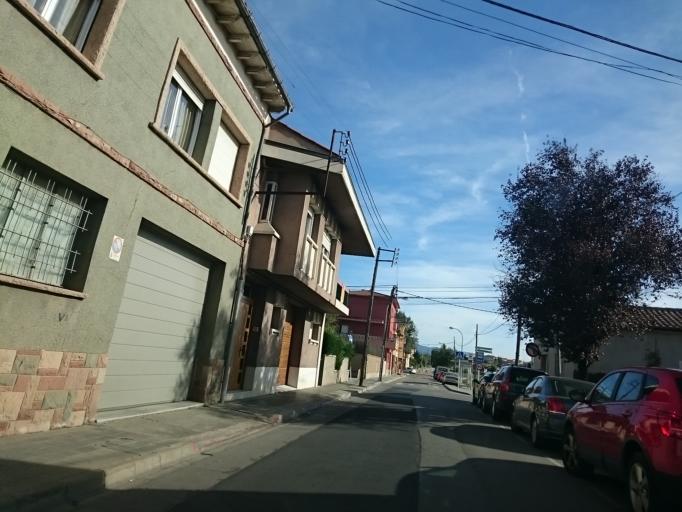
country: ES
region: Catalonia
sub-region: Provincia de Barcelona
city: Vic
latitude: 41.9199
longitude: 2.2547
